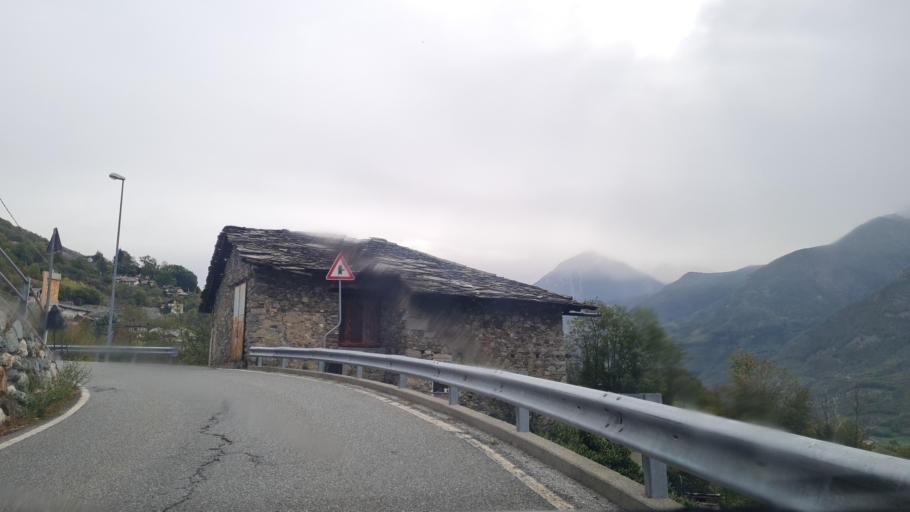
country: IT
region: Aosta Valley
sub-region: Valle d'Aosta
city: Quart
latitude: 45.7481
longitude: 7.4066
